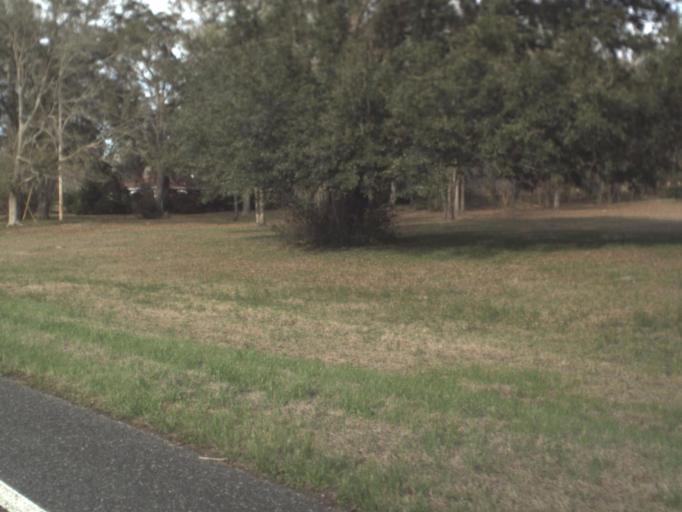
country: US
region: Florida
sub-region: Jefferson County
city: Monticello
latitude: 30.6131
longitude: -83.8721
